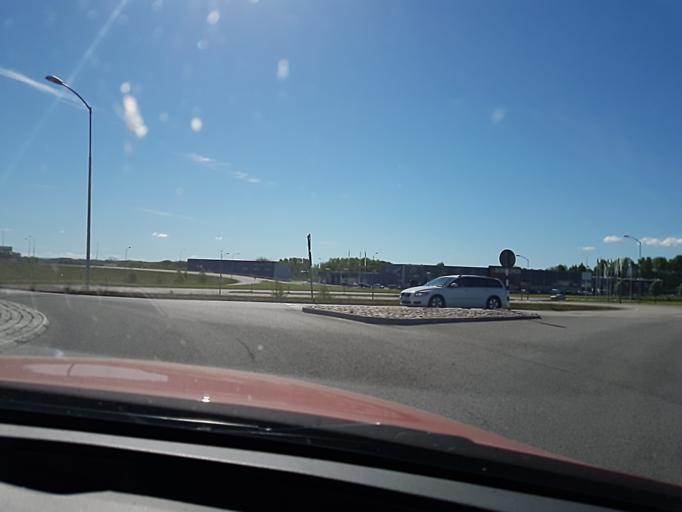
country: SE
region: Vaestra Goetaland
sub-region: Skovde Kommun
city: Skoevde
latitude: 58.4132
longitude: 13.8792
